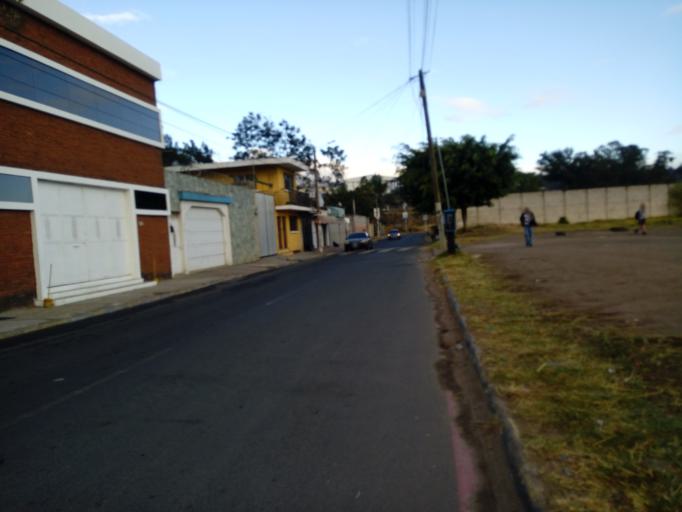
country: GT
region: Guatemala
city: Villa Nueva
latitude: 14.5356
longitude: -90.5836
